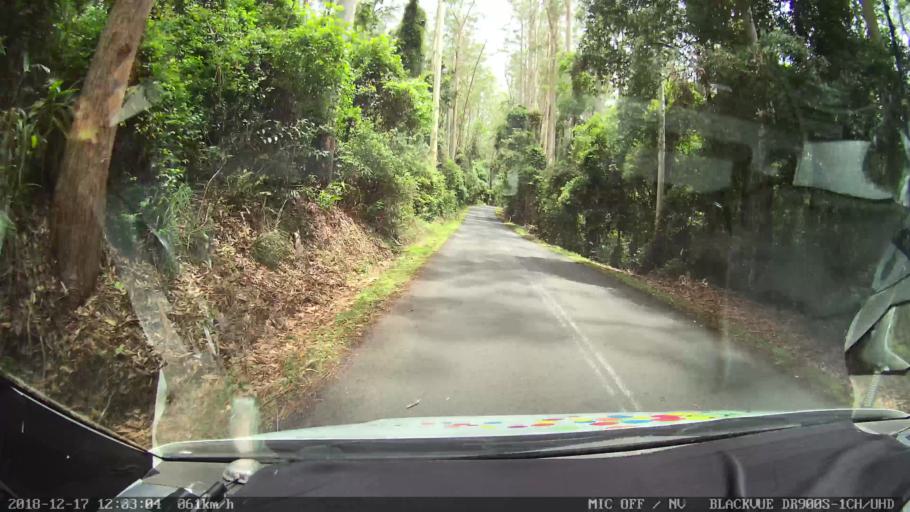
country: AU
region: New South Wales
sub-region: Kyogle
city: Kyogle
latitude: -28.5114
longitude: 152.5692
